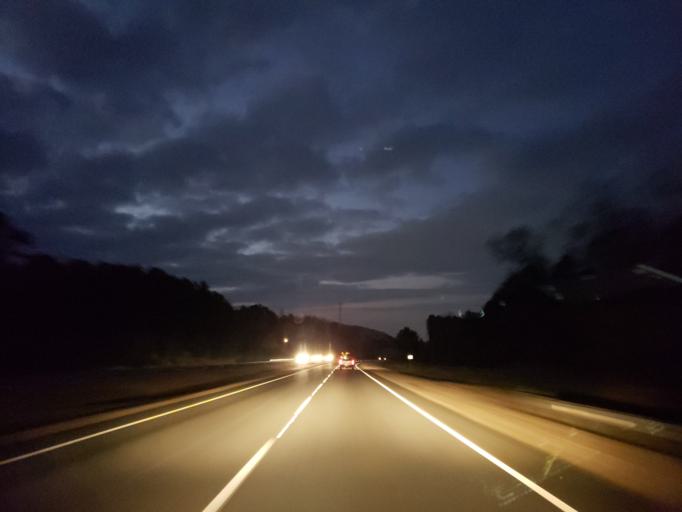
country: US
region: Georgia
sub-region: Polk County
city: Rockmart
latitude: 33.9679
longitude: -84.9971
